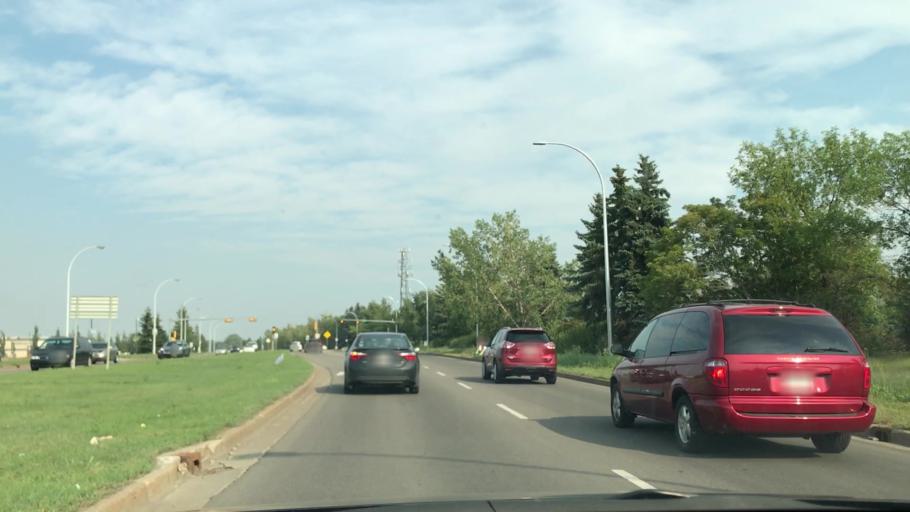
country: CA
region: Alberta
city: Edmonton
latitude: 53.4521
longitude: -113.4757
